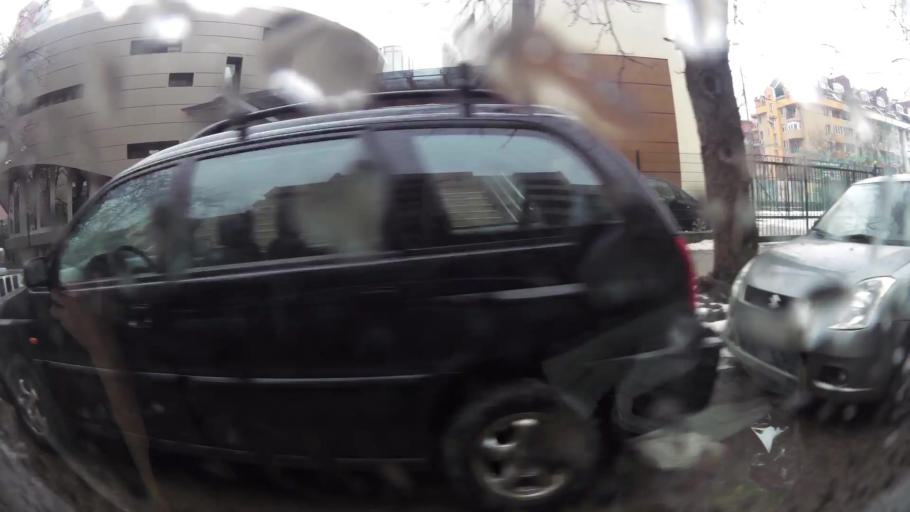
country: BG
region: Sofia-Capital
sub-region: Stolichna Obshtina
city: Sofia
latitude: 42.6763
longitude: 23.2940
